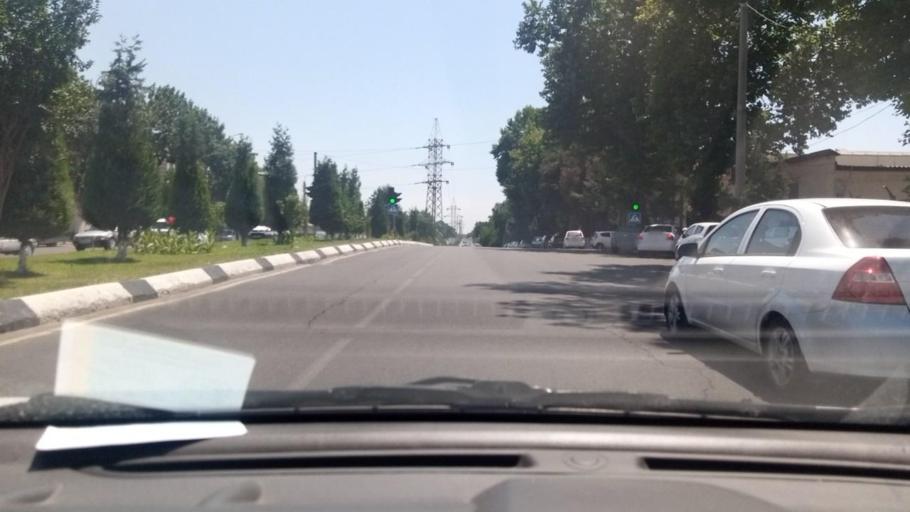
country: UZ
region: Toshkent Shahri
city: Tashkent
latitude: 41.3009
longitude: 69.1938
